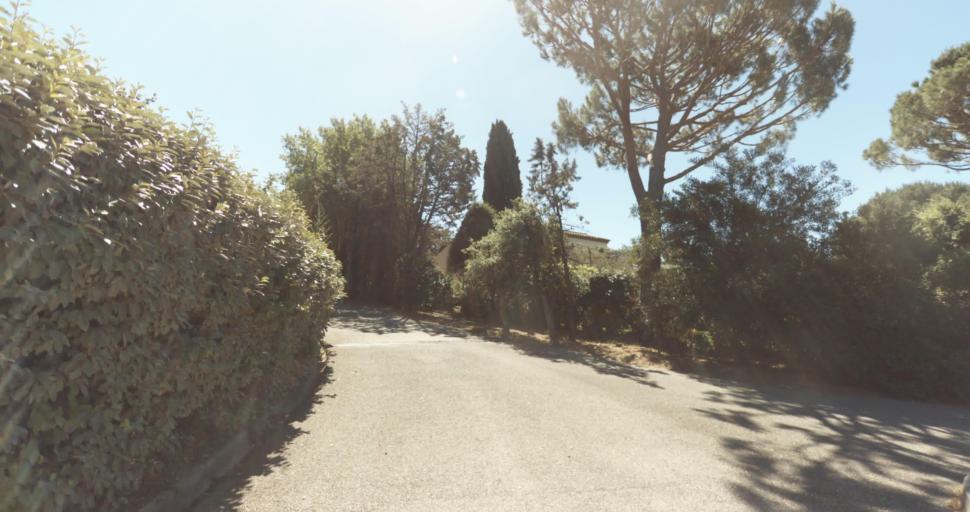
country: FR
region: Provence-Alpes-Cote d'Azur
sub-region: Departement du Var
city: Gassin
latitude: 43.2576
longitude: 6.5988
